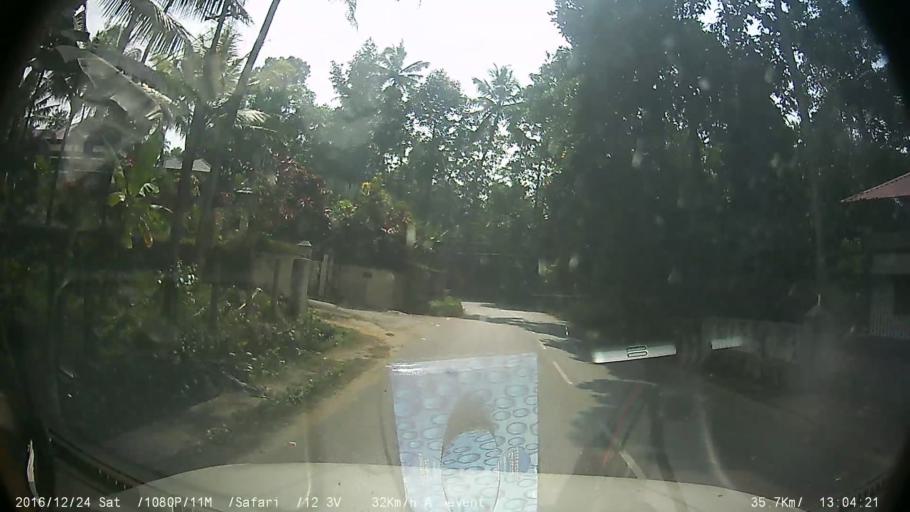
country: IN
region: Kerala
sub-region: Ernakulam
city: Muvattupuzha
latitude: 9.8900
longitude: 76.5936
